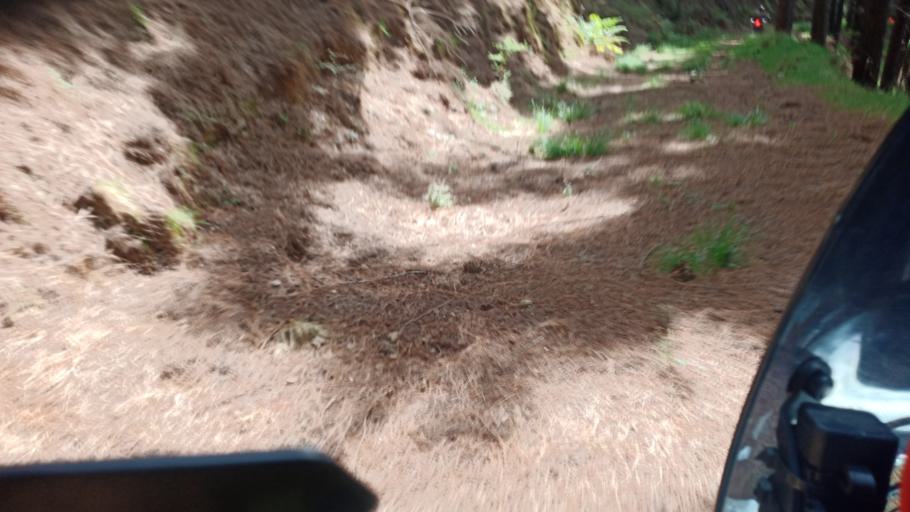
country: NZ
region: Gisborne
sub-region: Gisborne District
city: Gisborne
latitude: -38.4602
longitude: 177.9302
